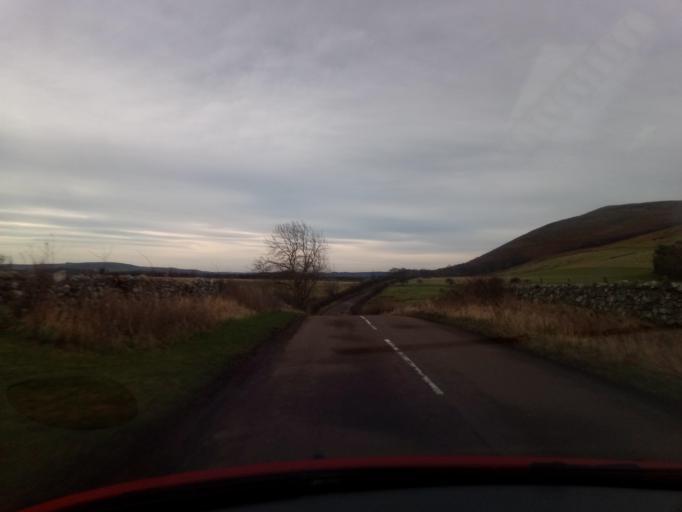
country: GB
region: England
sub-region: Northumberland
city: Kirknewton
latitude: 55.5661
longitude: -2.1014
